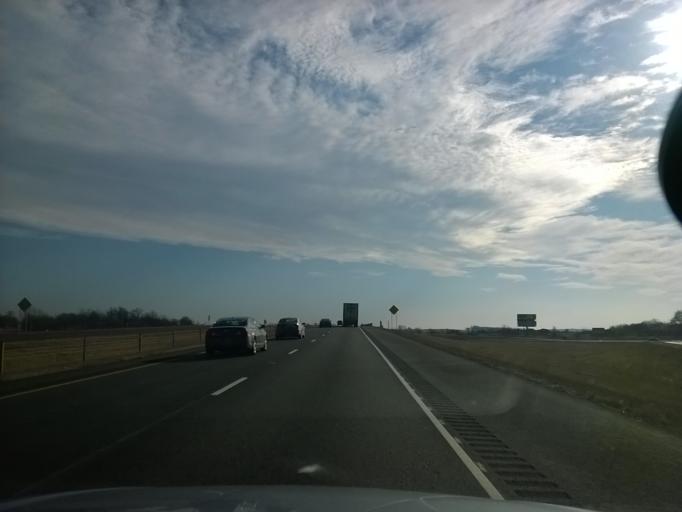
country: US
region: Indiana
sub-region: Johnson County
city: Edinburgh
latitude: 39.3649
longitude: -85.9427
